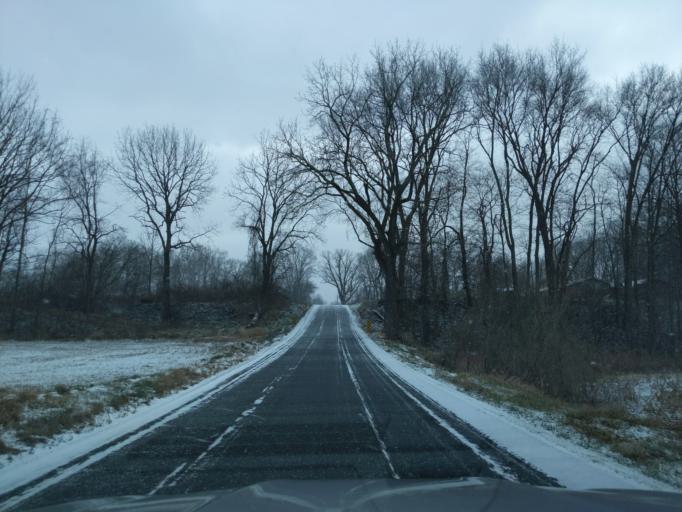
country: US
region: Indiana
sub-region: Decatur County
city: Westport
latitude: 39.2288
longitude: -85.5176
